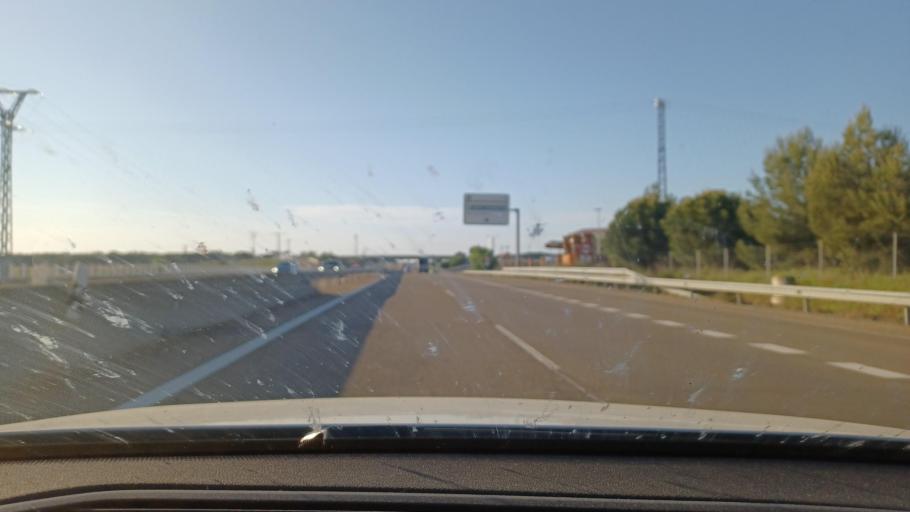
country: ES
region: Castille and Leon
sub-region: Provincia de Valladolid
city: Cisterniga
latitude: 41.5927
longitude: -4.6916
